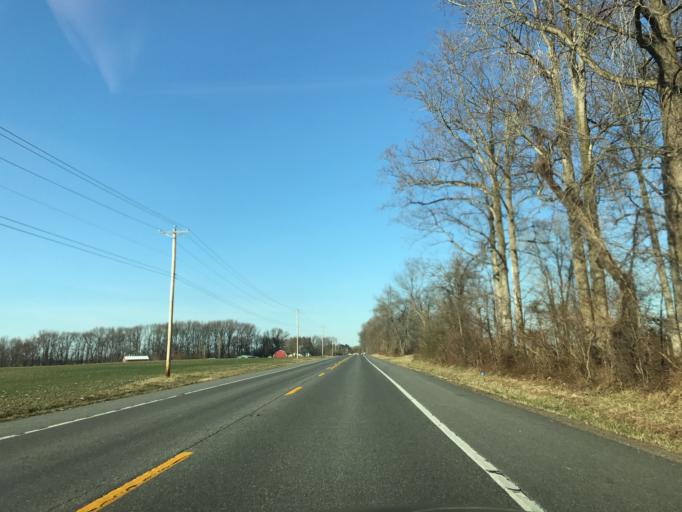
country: US
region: Maryland
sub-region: Queen Anne's County
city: Kingstown
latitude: 39.1708
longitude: -75.8597
